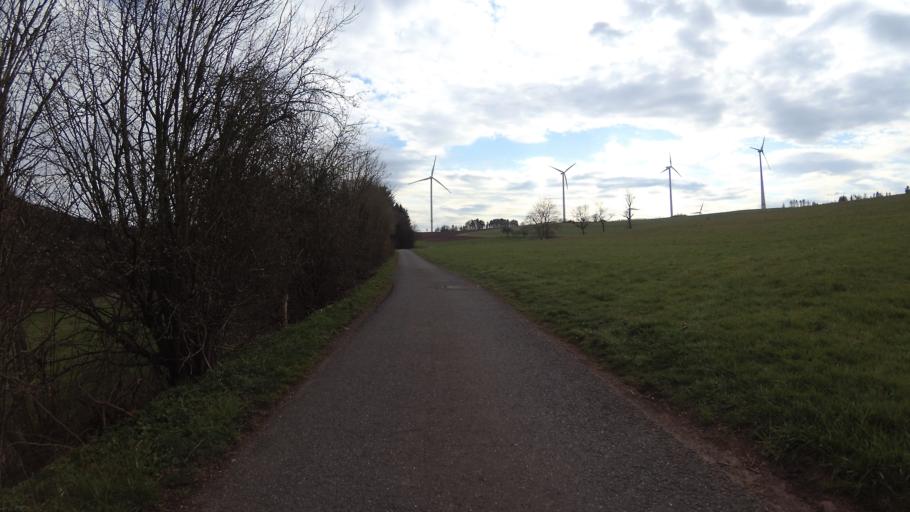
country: DE
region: Rheinland-Pfalz
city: Hahnweiler
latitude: 49.5705
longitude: 7.2205
